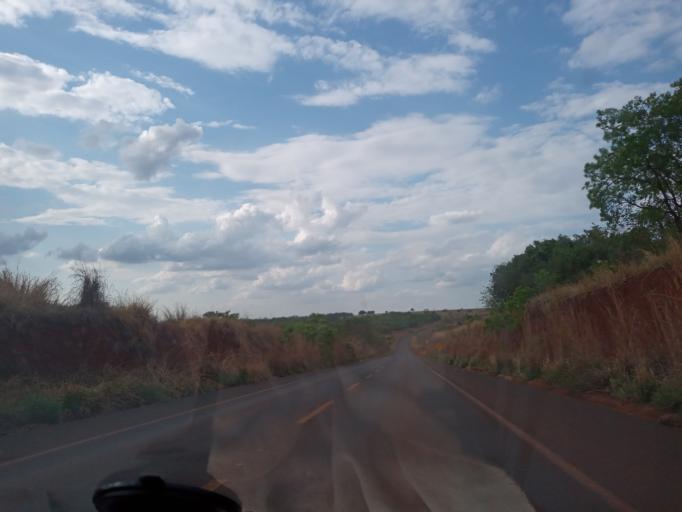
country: BR
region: Minas Gerais
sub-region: Ituiutaba
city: Ituiutaba
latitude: -19.1227
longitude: -49.5188
